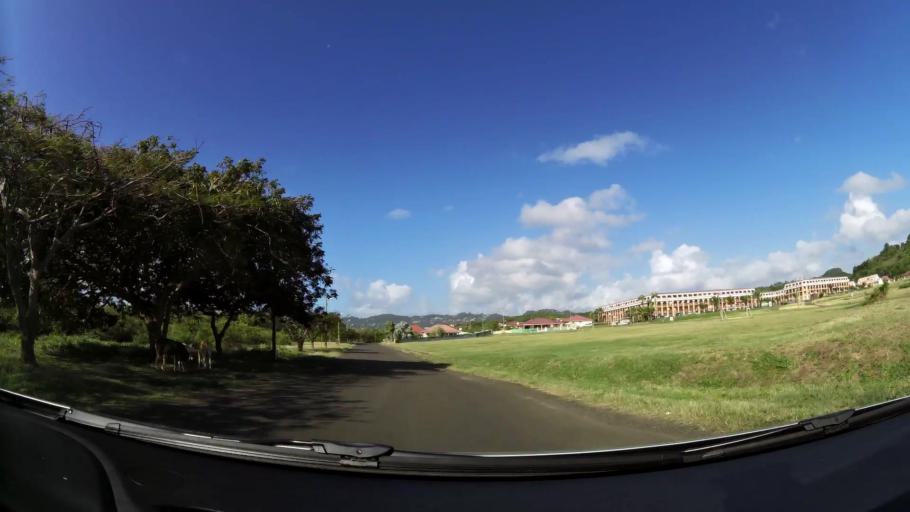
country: MQ
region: Martinique
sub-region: Martinique
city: Le Francois
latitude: 14.6201
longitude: -60.8992
